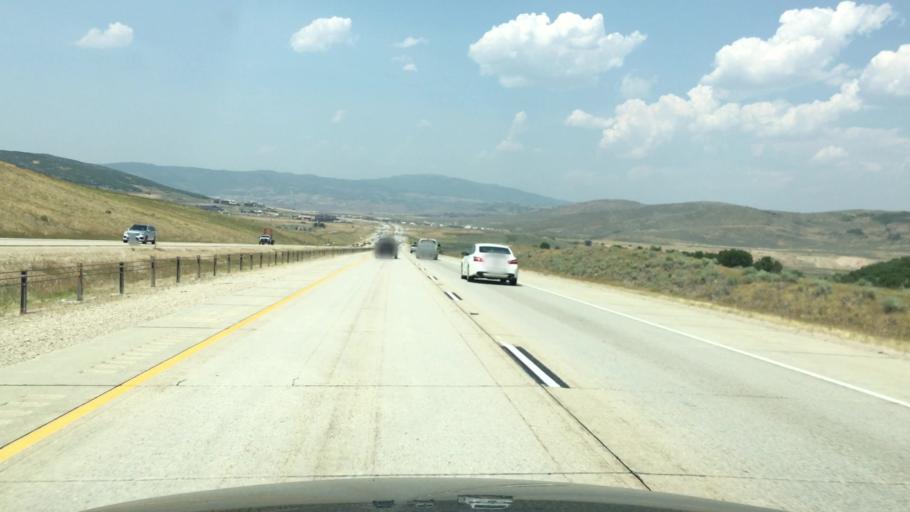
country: US
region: Utah
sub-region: Summit County
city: Park City
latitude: 40.6604
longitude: -111.4581
